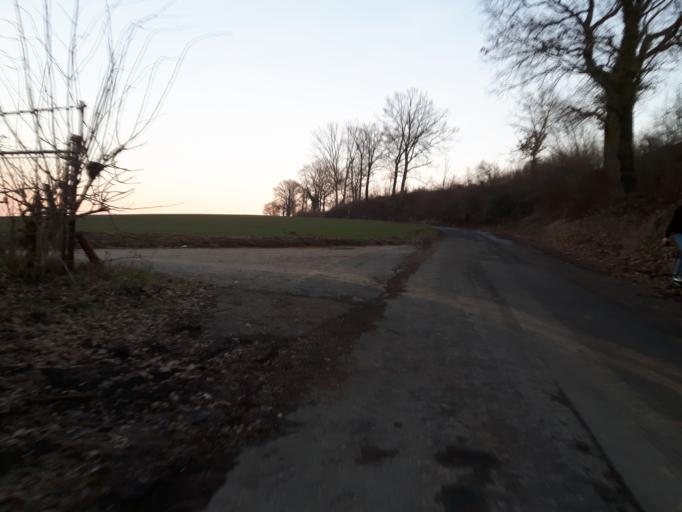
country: DE
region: Baden-Wuerttemberg
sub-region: Regierungsbezirk Stuttgart
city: Schwaigern
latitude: 49.1625
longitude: 9.0716
